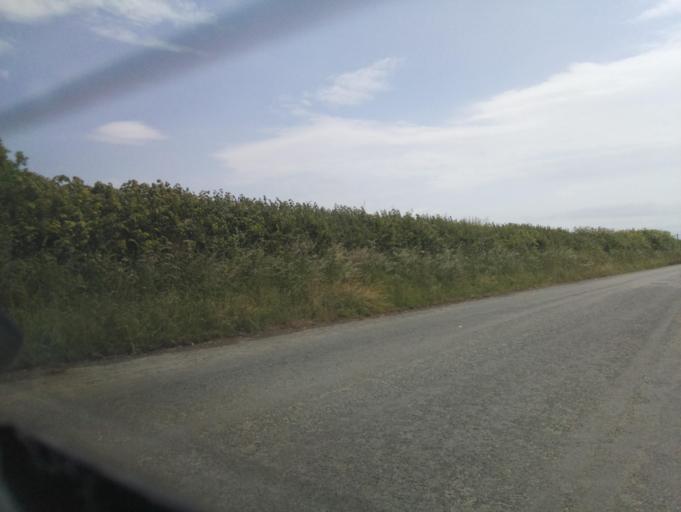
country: GB
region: Wales
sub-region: Vale of Glamorgan
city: Wick
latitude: 51.4144
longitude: -3.5479
